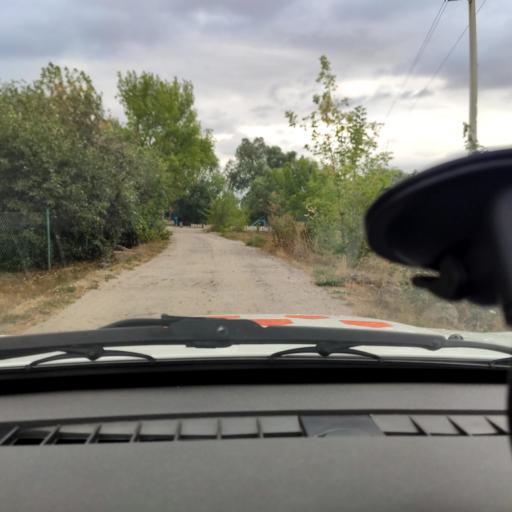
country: RU
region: Voronezj
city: Novaya Usman'
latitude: 51.6198
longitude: 39.4060
